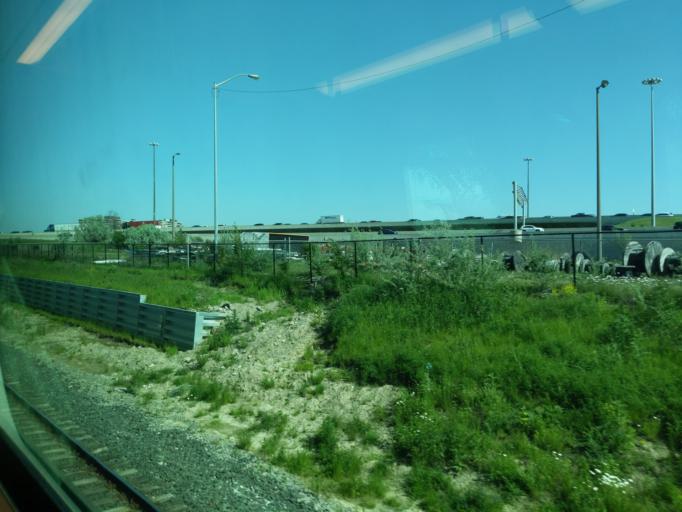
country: CA
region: Ontario
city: Etobicoke
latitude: 43.7064
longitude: -79.5595
